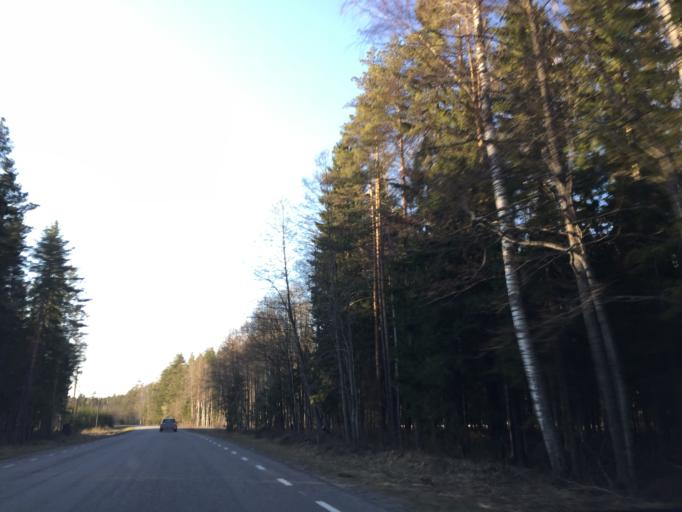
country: EE
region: Ida-Virumaa
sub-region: Toila vald
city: Voka
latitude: 59.1531
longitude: 27.6059
